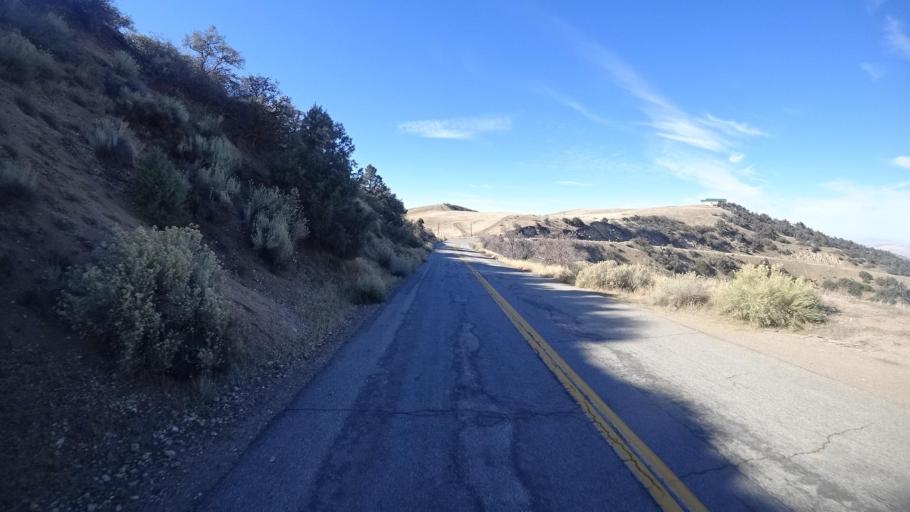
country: US
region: California
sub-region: Kern County
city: Pine Mountain Club
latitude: 34.8724
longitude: -119.3374
